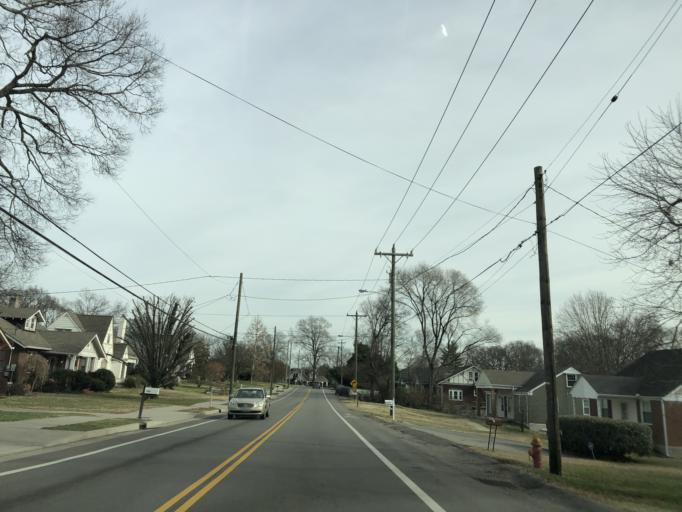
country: US
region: Tennessee
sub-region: Davidson County
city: Nashville
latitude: 36.2101
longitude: -86.7272
